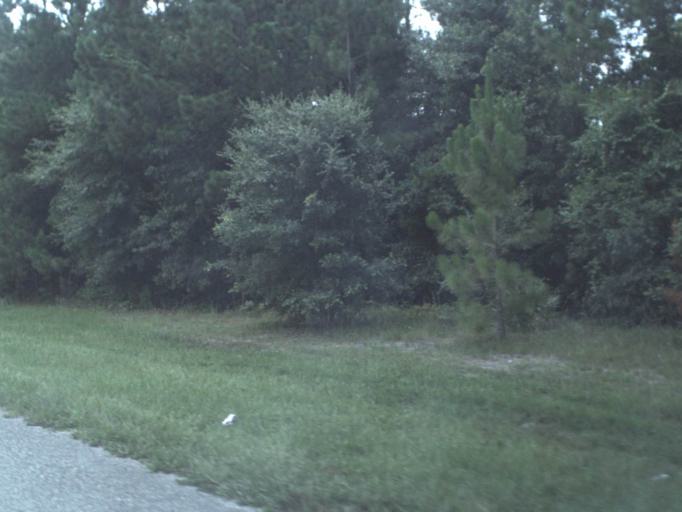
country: US
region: Florida
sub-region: Saint Johns County
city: Palm Valley
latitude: 30.0933
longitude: -81.4675
